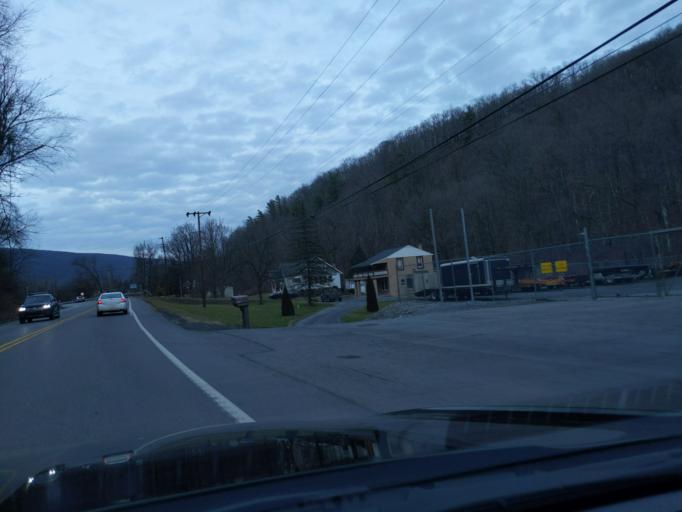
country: US
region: Pennsylvania
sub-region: Blair County
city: Lakemont
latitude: 40.4497
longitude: -78.3529
